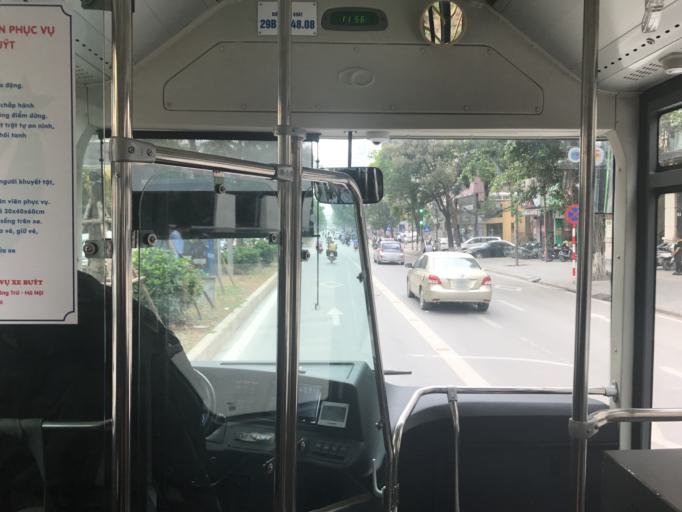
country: VN
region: Ha Noi
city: Dong Da
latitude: 21.0224
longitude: 105.8189
